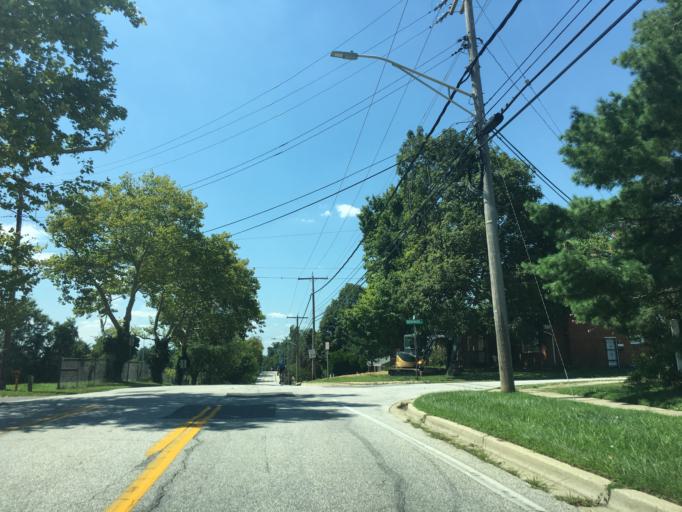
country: US
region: Maryland
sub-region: Anne Arundel County
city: Linthicum
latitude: 39.1980
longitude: -76.6647
